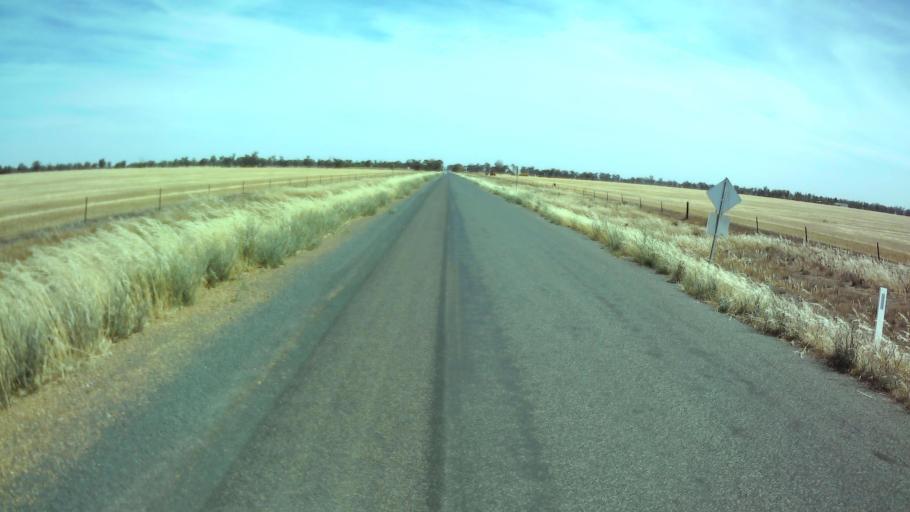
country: AU
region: New South Wales
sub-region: Weddin
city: Grenfell
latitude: -33.9856
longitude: 147.7771
